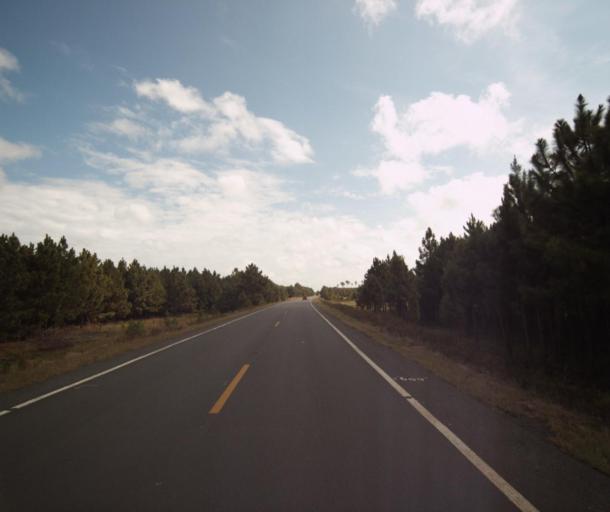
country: BR
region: Rio Grande do Sul
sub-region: Sao Lourenco Do Sul
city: Sao Lourenco do Sul
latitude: -31.4432
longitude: -51.2020
